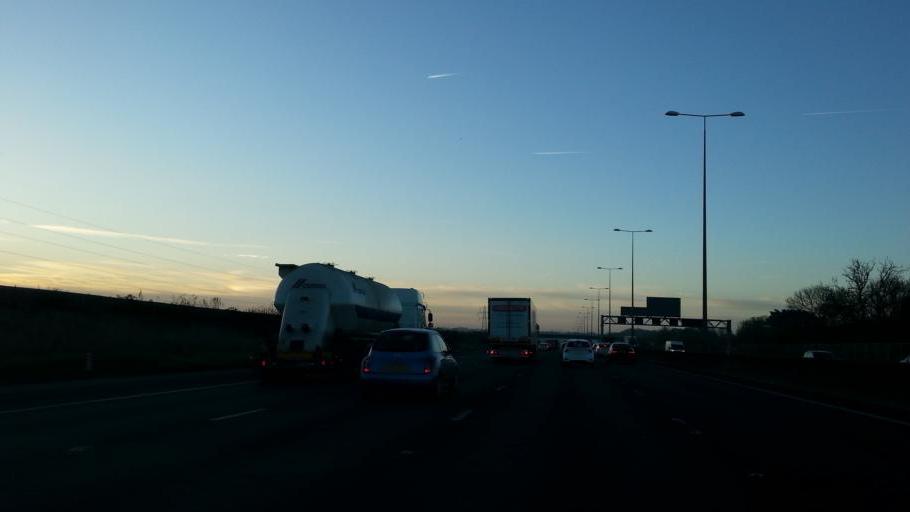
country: GB
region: England
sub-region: Hertfordshire
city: Redbourn
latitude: 51.8071
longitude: -0.4146
